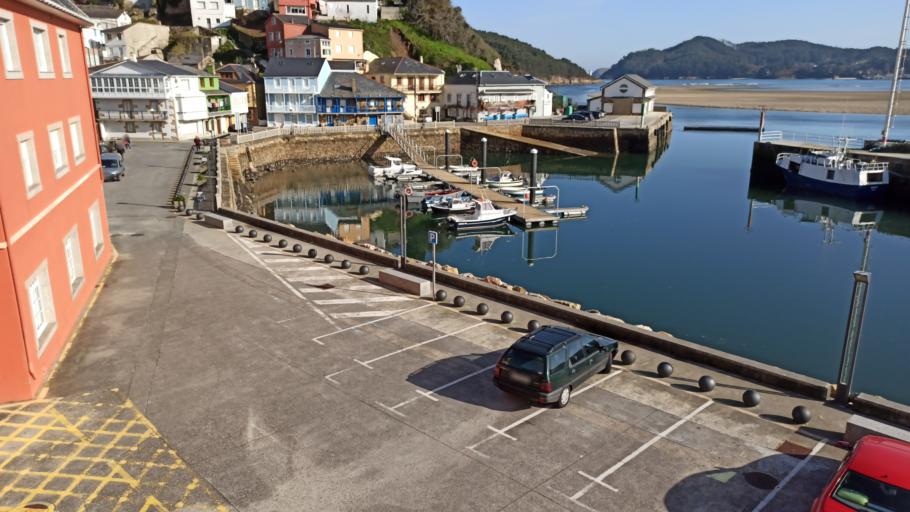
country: ES
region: Galicia
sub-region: Provincia da Coruna
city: Manon
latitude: 43.7372
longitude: -7.7014
